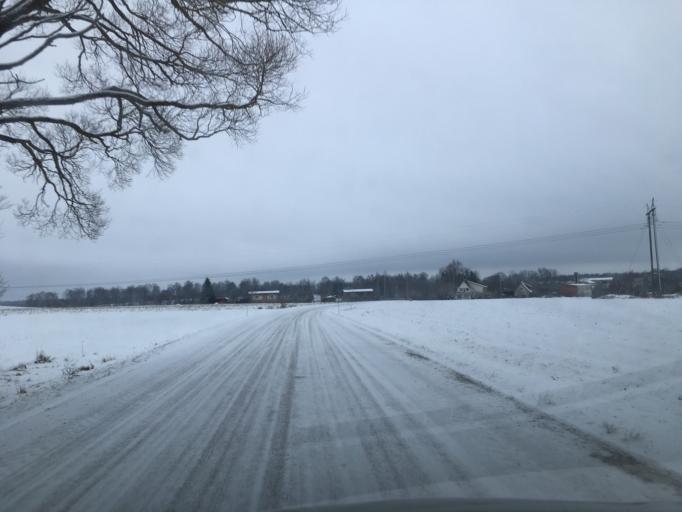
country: EE
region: Tartu
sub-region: Elva linn
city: Elva
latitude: 58.1885
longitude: 26.3369
